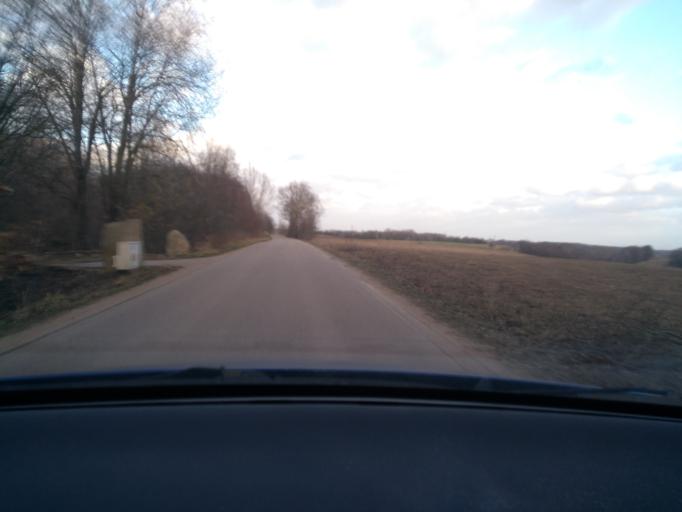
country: PL
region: Pomeranian Voivodeship
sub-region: Powiat kartuski
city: Przodkowo
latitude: 54.4134
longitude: 18.2685
